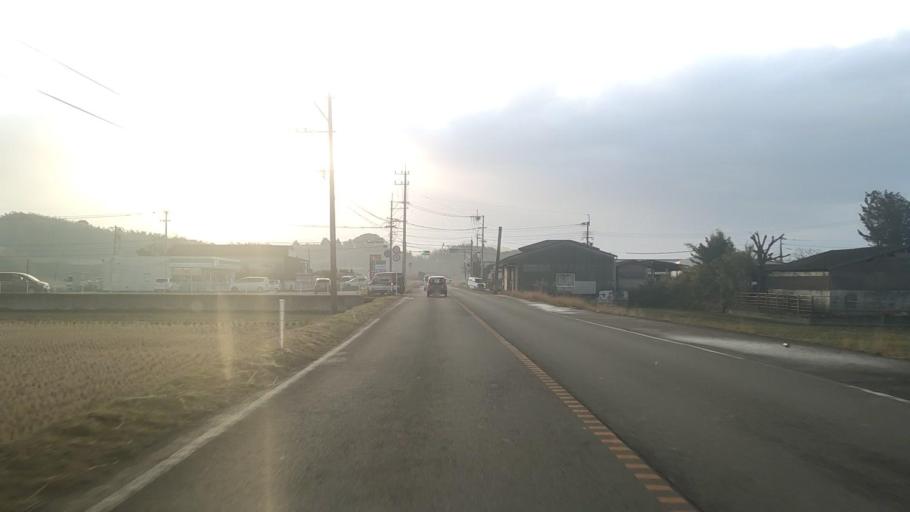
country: JP
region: Kumamoto
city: Uto
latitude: 32.7249
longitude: 130.7662
